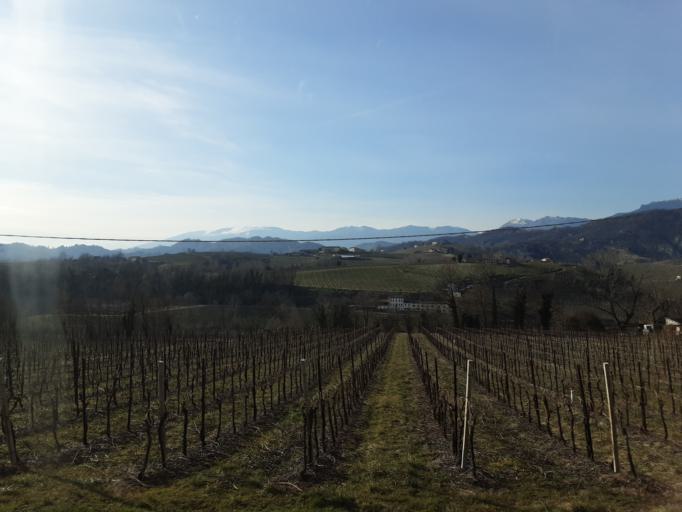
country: IT
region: Veneto
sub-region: Provincia di Treviso
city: Carpesica
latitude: 45.9505
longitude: 12.2785
